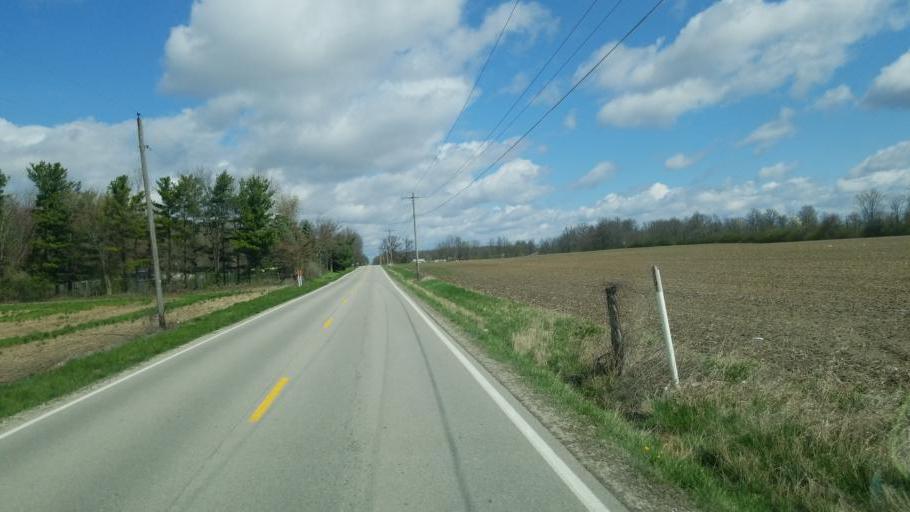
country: US
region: Ohio
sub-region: Delaware County
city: Delaware
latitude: 40.3021
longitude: -83.1265
